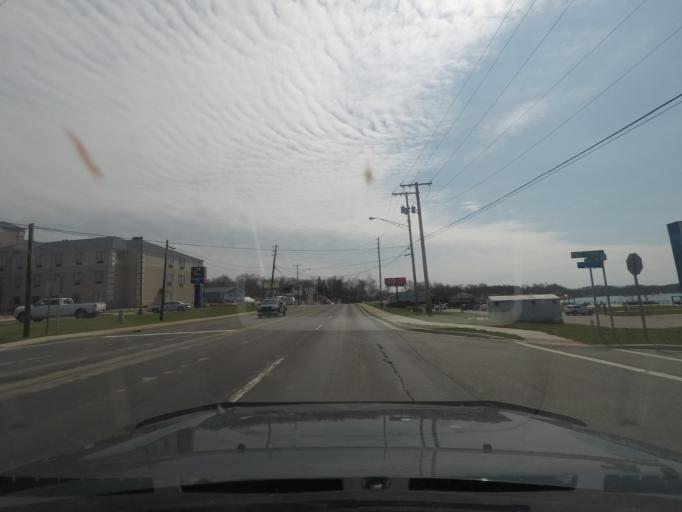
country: US
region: Indiana
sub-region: LaPorte County
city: LaPorte
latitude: 41.6301
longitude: -86.7384
